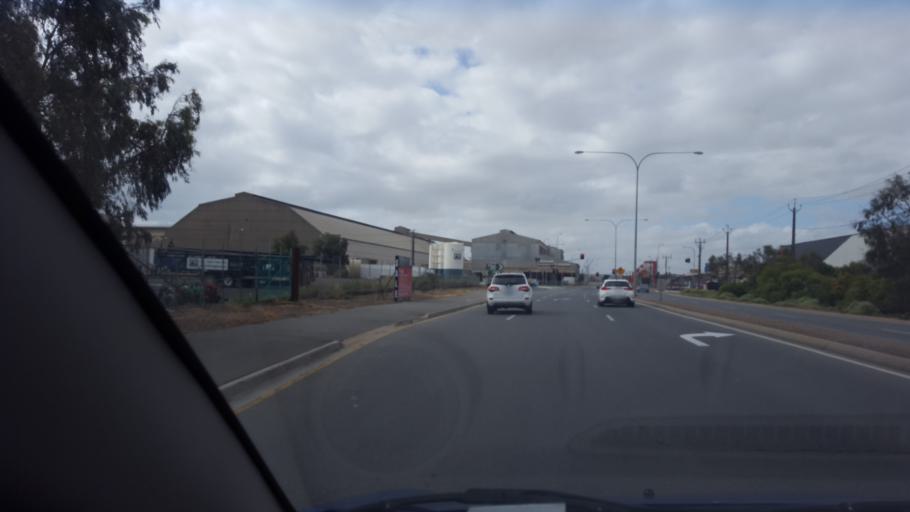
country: AU
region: South Australia
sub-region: Port Adelaide Enfield
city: Birkenhead
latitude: -34.8426
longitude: 138.5148
